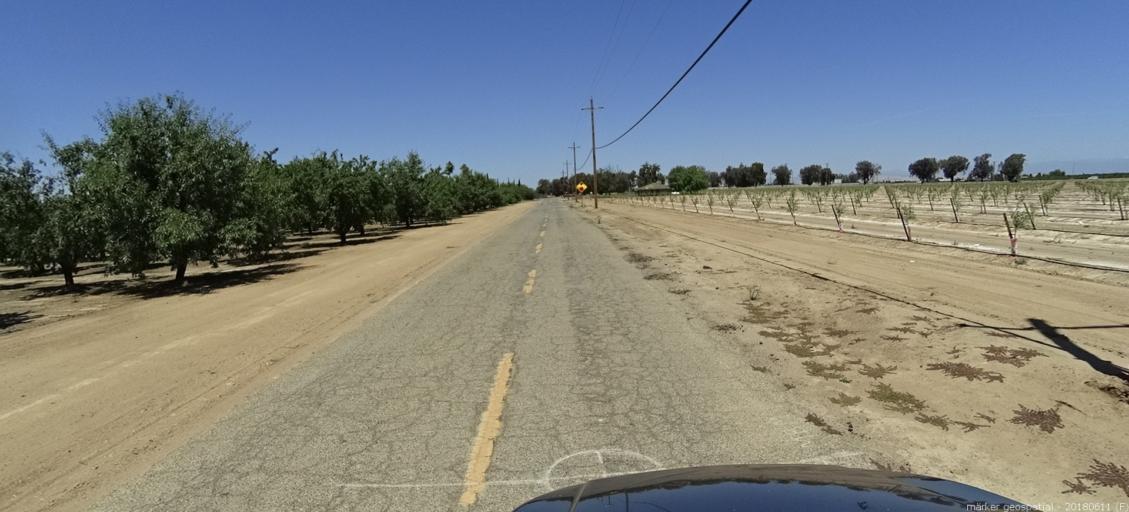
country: US
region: California
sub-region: Madera County
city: Fairmead
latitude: 37.0809
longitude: -120.2115
